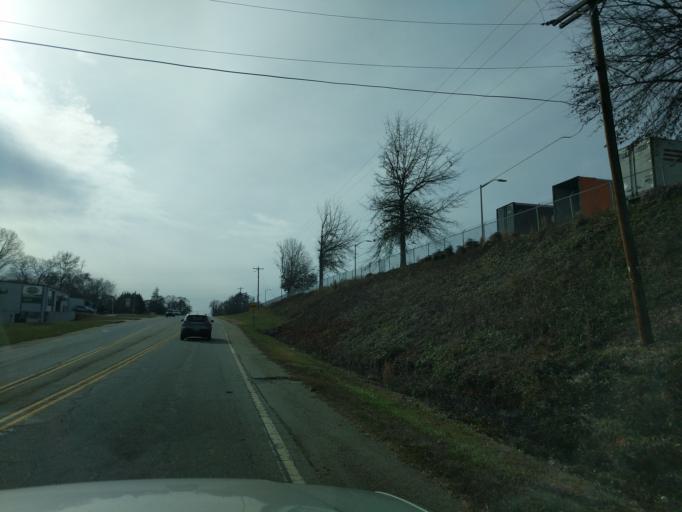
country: US
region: South Carolina
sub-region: Oconee County
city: Walhalla
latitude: 34.7658
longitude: -83.0346
